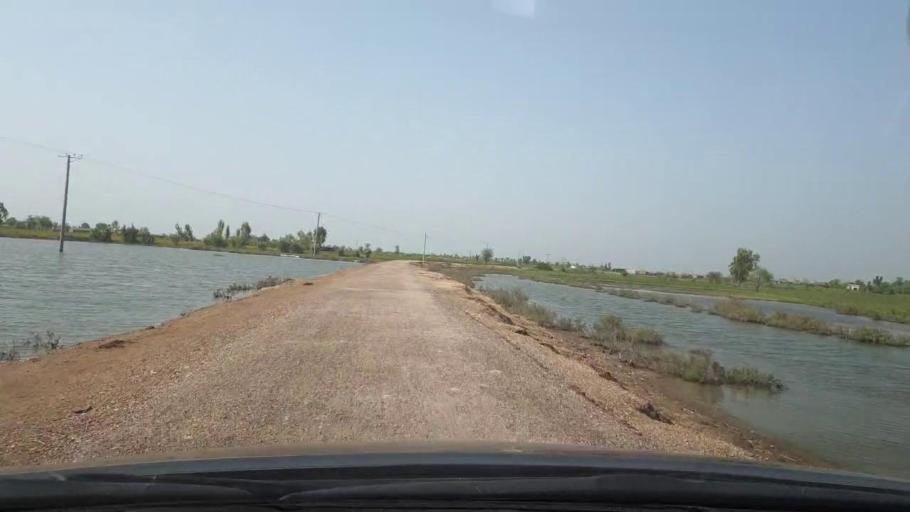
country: PK
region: Sindh
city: Tando Bago
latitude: 24.7123
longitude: 69.0882
